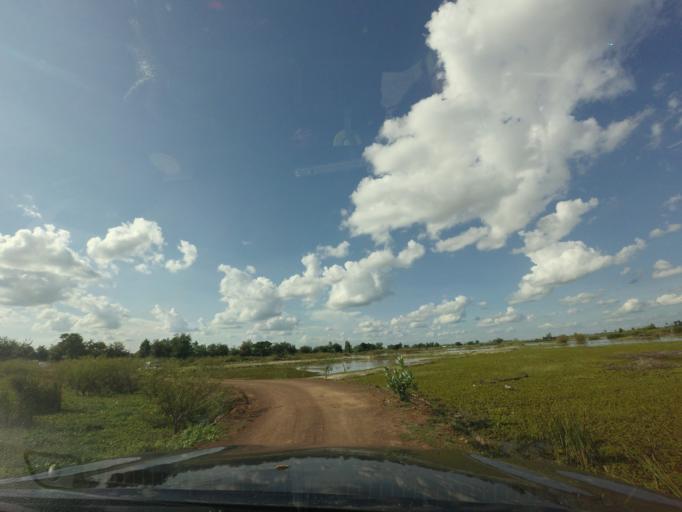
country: TH
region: Changwat Udon Thani
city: Ban Dung
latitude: 17.7450
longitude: 103.3581
